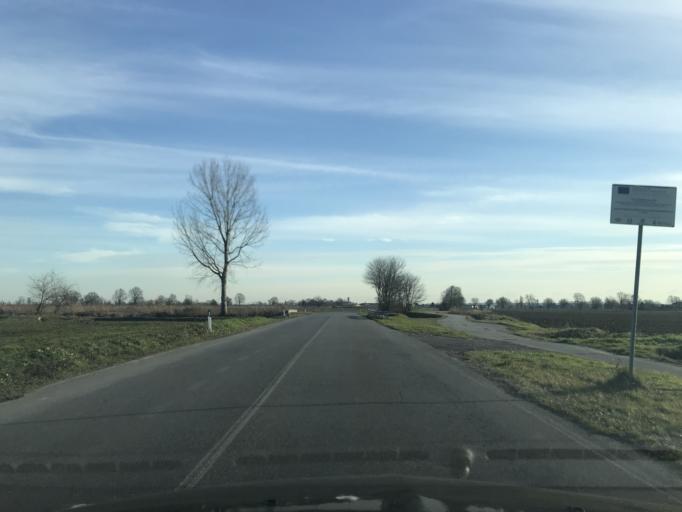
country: IT
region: Lombardy
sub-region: Provincia di Lodi
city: Bargano
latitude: 45.2548
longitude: 9.4331
